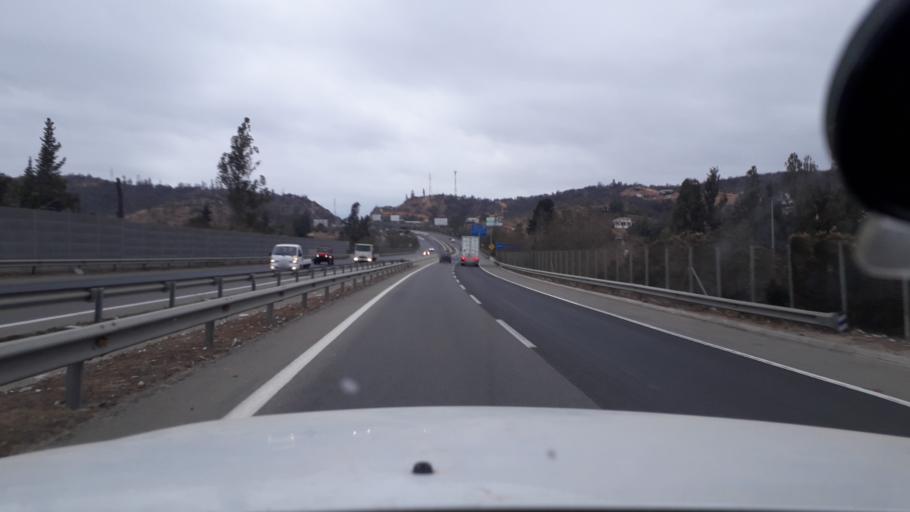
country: CL
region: Valparaiso
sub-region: Provincia de Marga Marga
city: Villa Alemana
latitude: -33.0563
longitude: -71.3387
